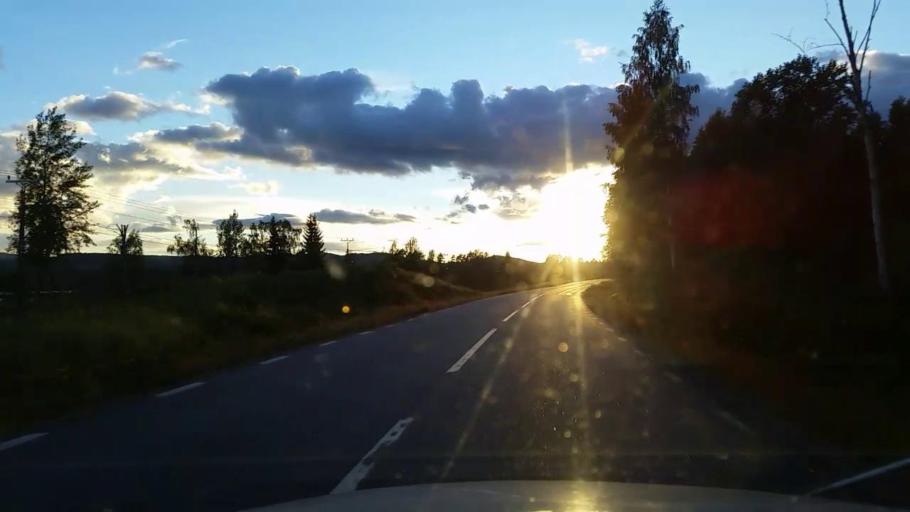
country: SE
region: Gaevleborg
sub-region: Ljusdals Kommun
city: Farila
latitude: 62.1310
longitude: 15.7000
